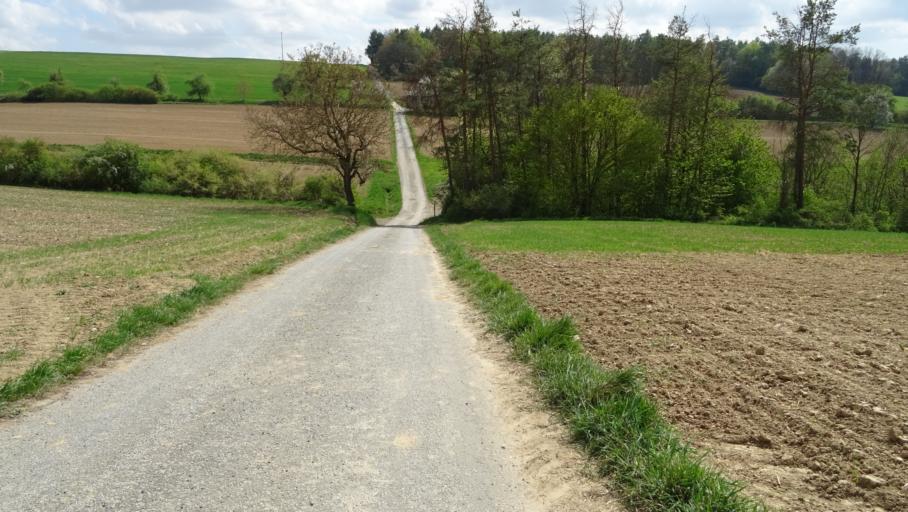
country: DE
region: Baden-Wuerttemberg
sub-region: Karlsruhe Region
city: Billigheim
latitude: 49.4051
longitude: 9.2413
